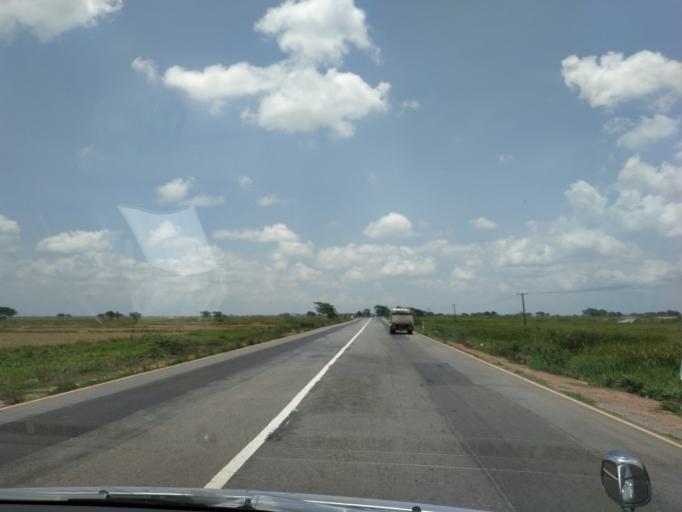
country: MM
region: Bago
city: Bago
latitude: 17.4639
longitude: 96.5905
